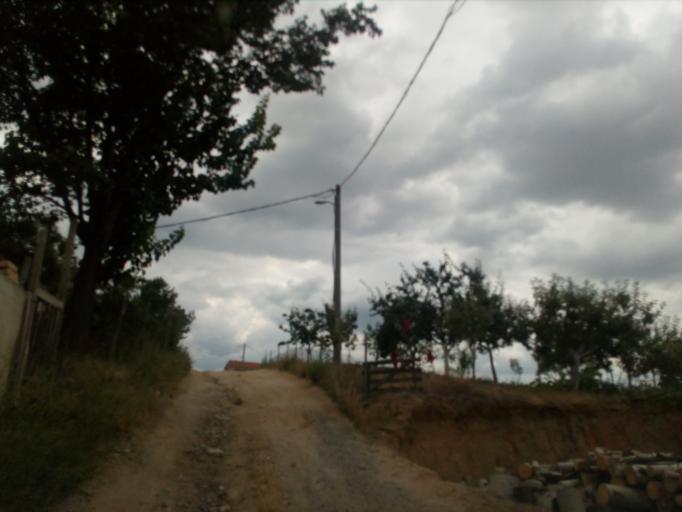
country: MK
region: Veles
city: Veles
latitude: 41.7091
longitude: 21.7586
